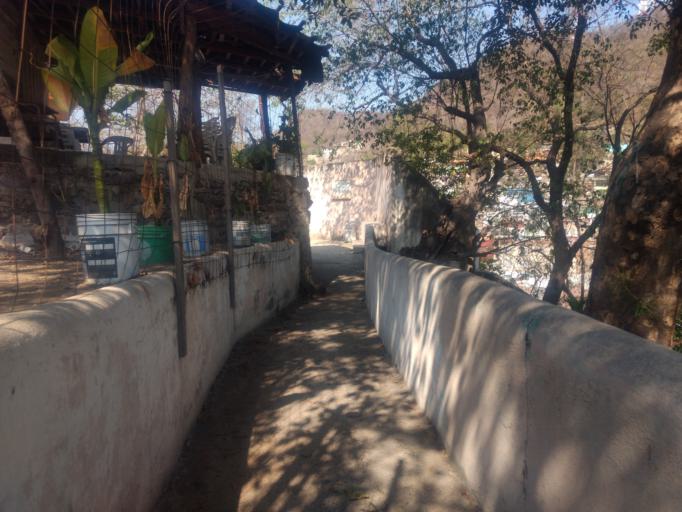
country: MX
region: Colima
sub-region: Manzanillo
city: Manzanillo
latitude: 19.0526
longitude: -104.3169
